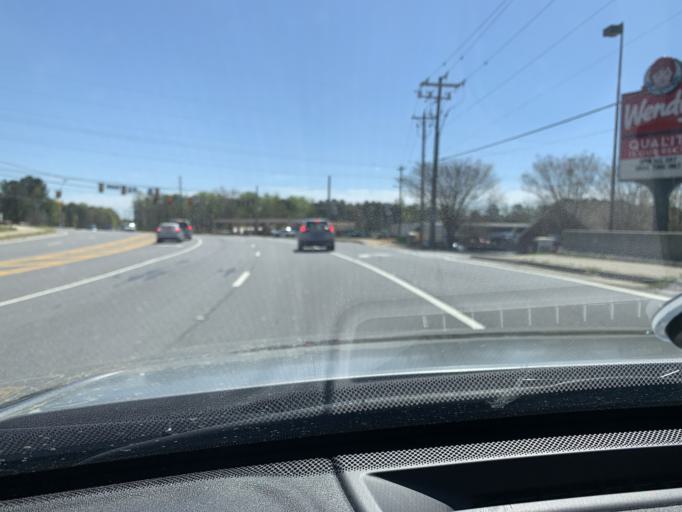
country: US
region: Georgia
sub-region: Fulton County
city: Milton
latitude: 34.1598
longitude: -84.2366
